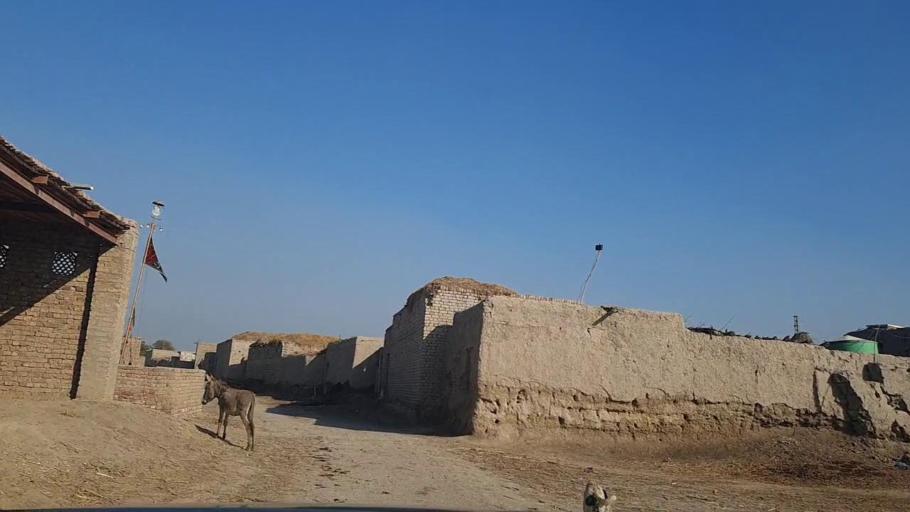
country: PK
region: Sindh
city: Daur
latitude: 26.3177
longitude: 68.1761
